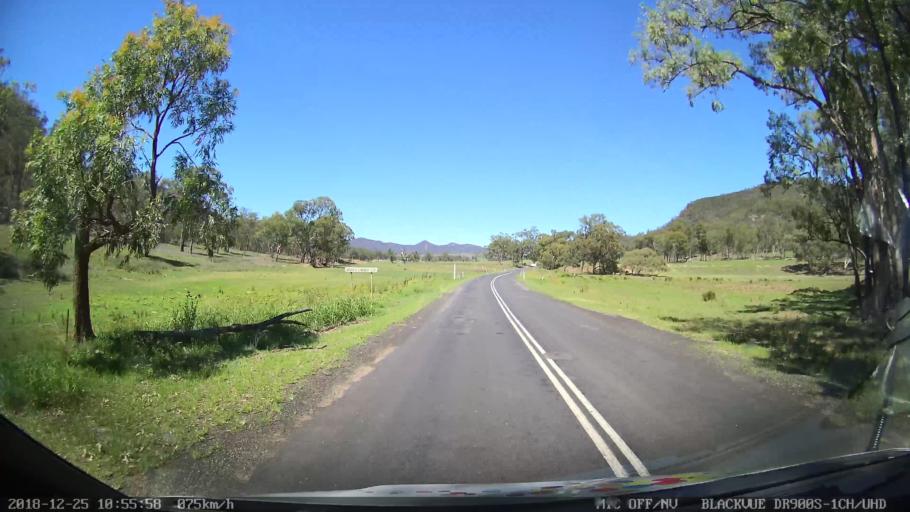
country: AU
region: New South Wales
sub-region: Upper Hunter Shire
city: Merriwa
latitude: -32.3991
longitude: 150.2678
